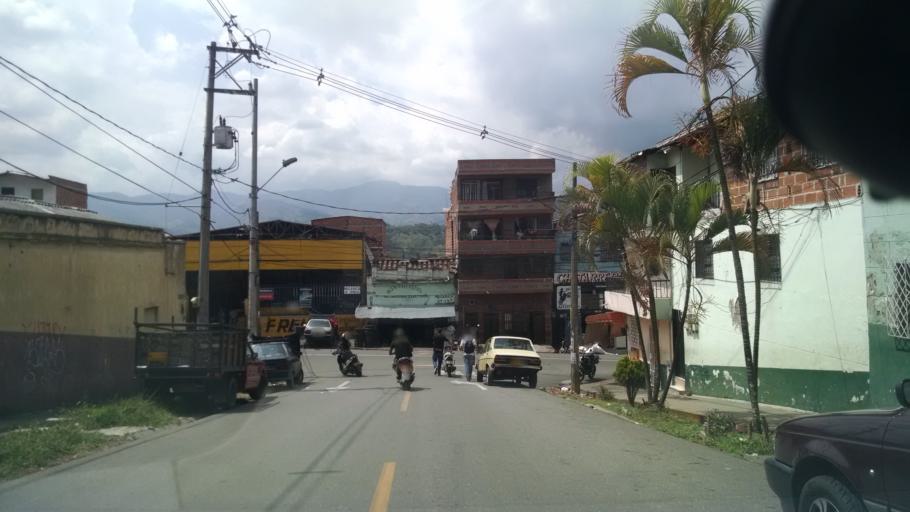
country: CO
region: Antioquia
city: Medellin
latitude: 6.2653
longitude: -75.5599
